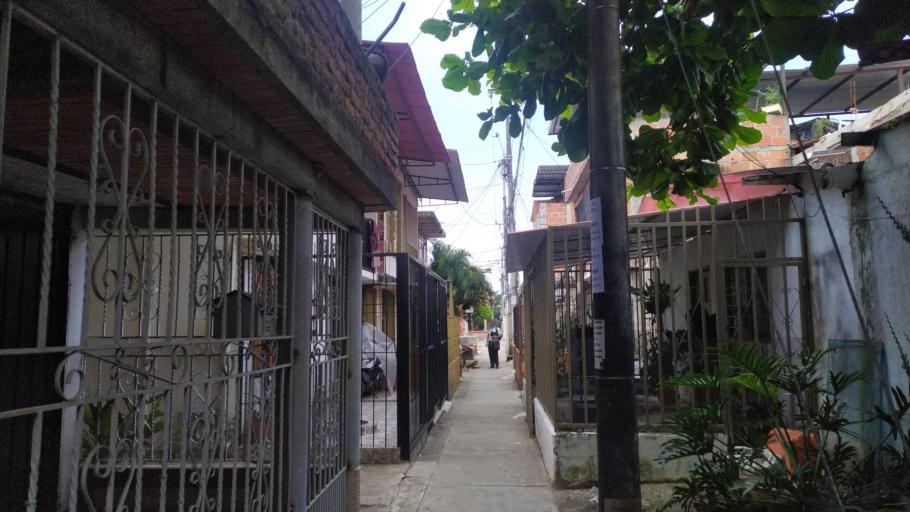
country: CO
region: Valle del Cauca
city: Jamundi
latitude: 3.2518
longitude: -76.5432
